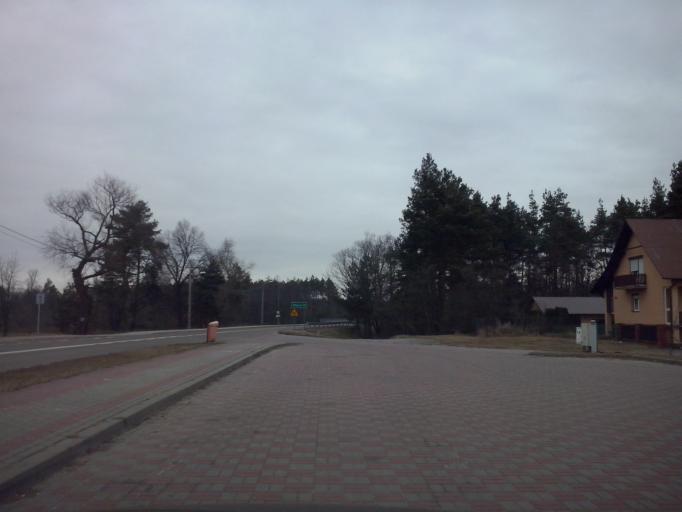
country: PL
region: Subcarpathian Voivodeship
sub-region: Powiat nizanski
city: Harasiuki
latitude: 50.4759
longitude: 22.4733
